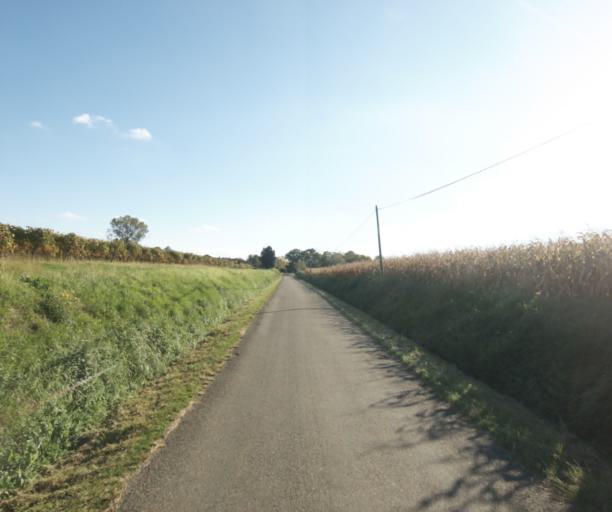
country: FR
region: Midi-Pyrenees
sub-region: Departement du Gers
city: Eauze
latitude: 43.7981
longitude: 0.1347
